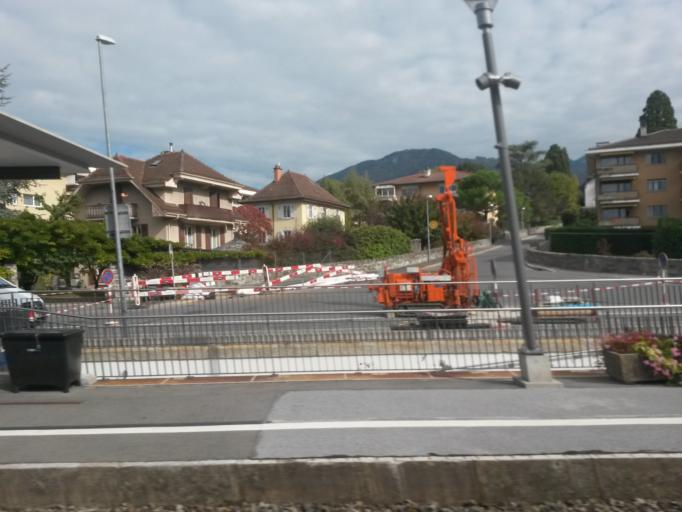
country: CH
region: Vaud
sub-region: Riviera-Pays-d'Enhaut District
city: La Tour-de-Peilz
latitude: 46.4552
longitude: 6.8599
